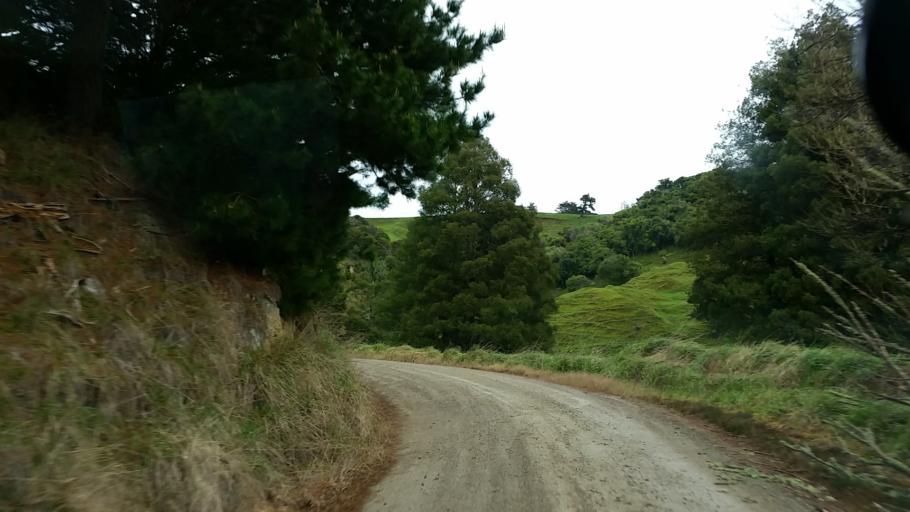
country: NZ
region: Taranaki
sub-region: South Taranaki District
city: Patea
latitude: -39.7578
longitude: 174.7076
